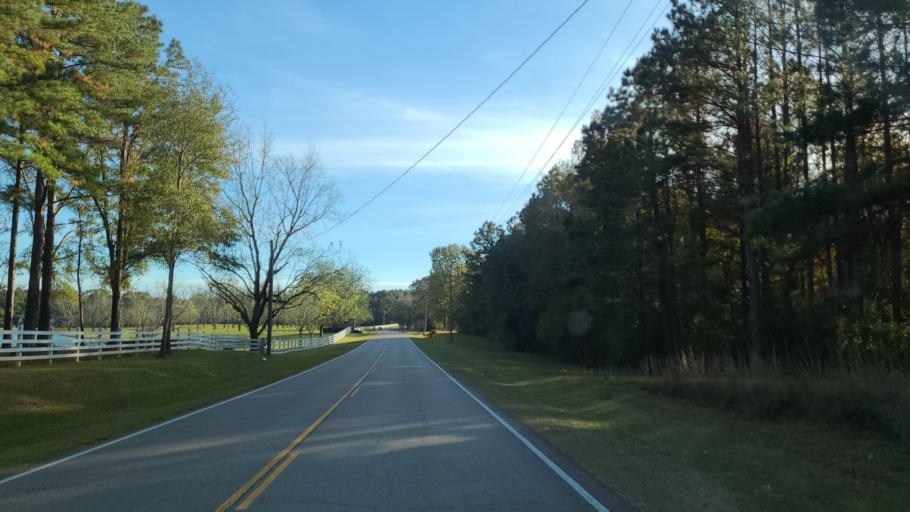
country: US
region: Mississippi
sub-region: Lamar County
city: Purvis
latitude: 31.1830
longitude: -89.2919
